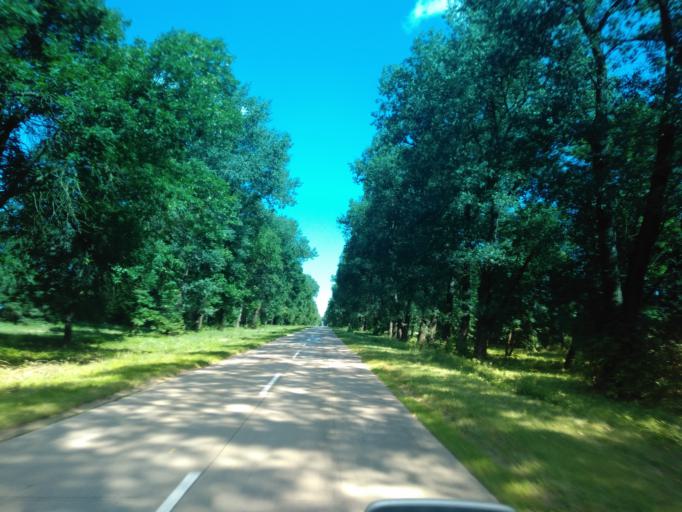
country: BY
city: Fanipol
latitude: 53.6597
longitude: 27.3238
